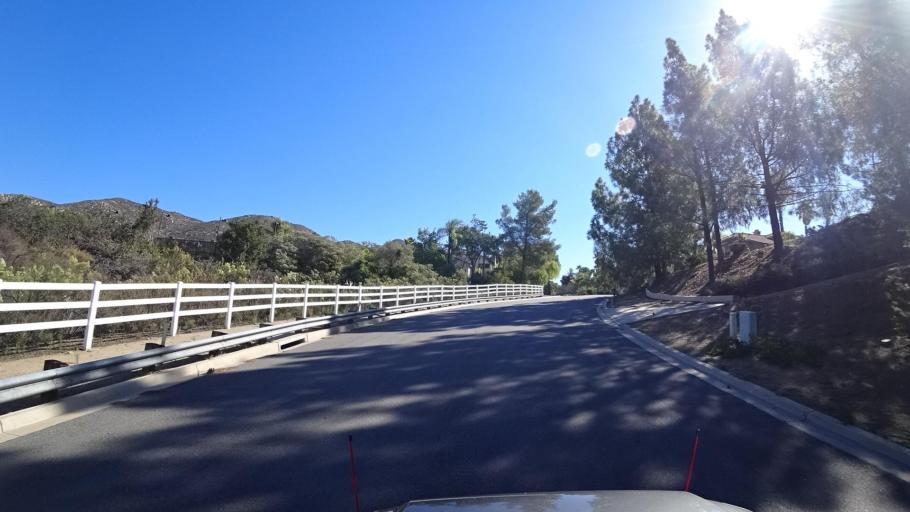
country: US
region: California
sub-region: San Diego County
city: Jamul
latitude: 32.7385
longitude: -116.8565
